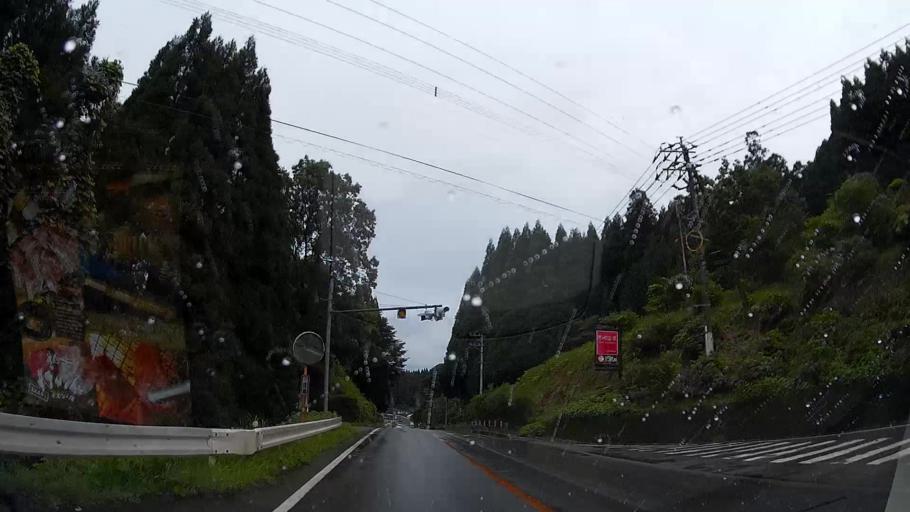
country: JP
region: Oita
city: Tsukawaki
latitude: 33.1308
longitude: 131.0632
